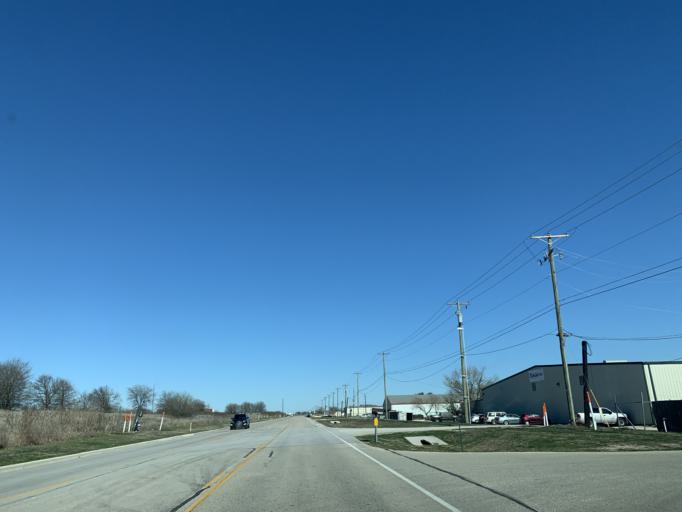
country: US
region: Texas
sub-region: Williamson County
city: Hutto
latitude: 30.5452
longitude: -97.5732
